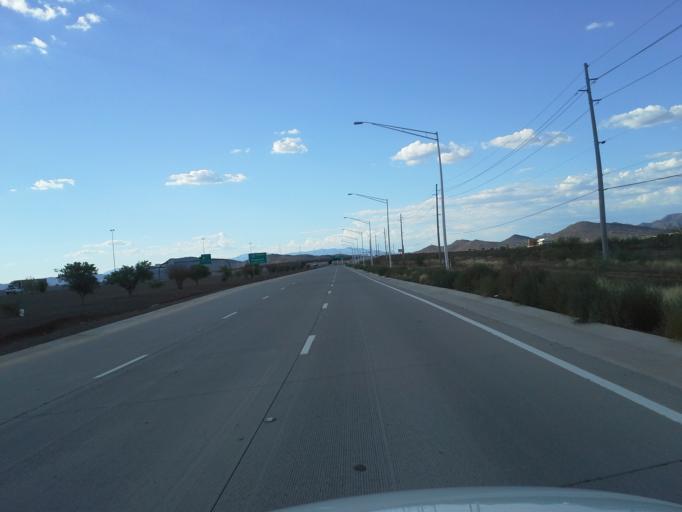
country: US
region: Arizona
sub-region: Maricopa County
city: Anthem
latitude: 33.7748
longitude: -112.1293
